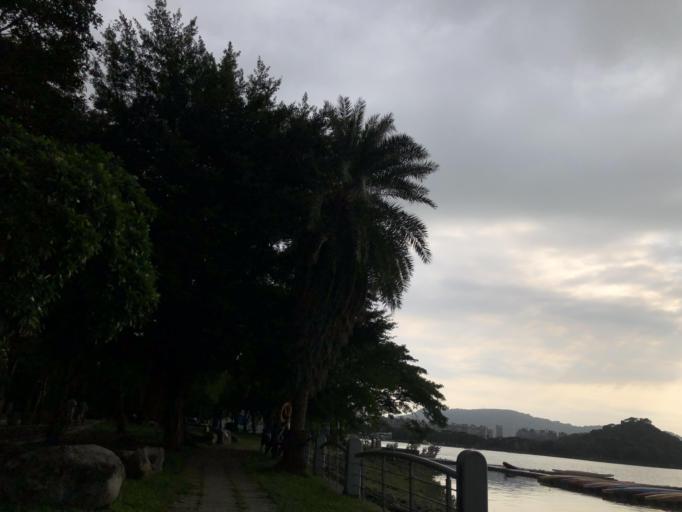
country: TW
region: Kaohsiung
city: Kaohsiung
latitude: 22.6838
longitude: 120.2987
